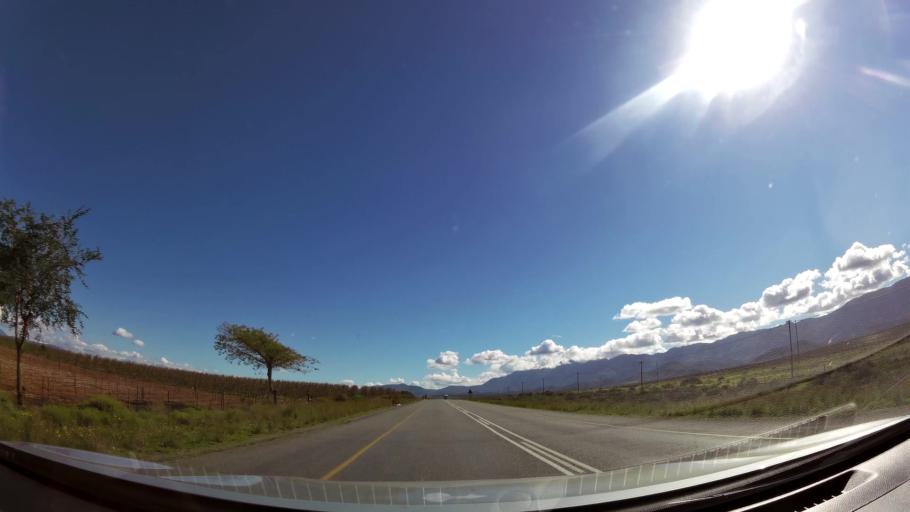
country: ZA
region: Western Cape
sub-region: Cape Winelands District Municipality
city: Ashton
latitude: -33.8367
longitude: 20.0049
